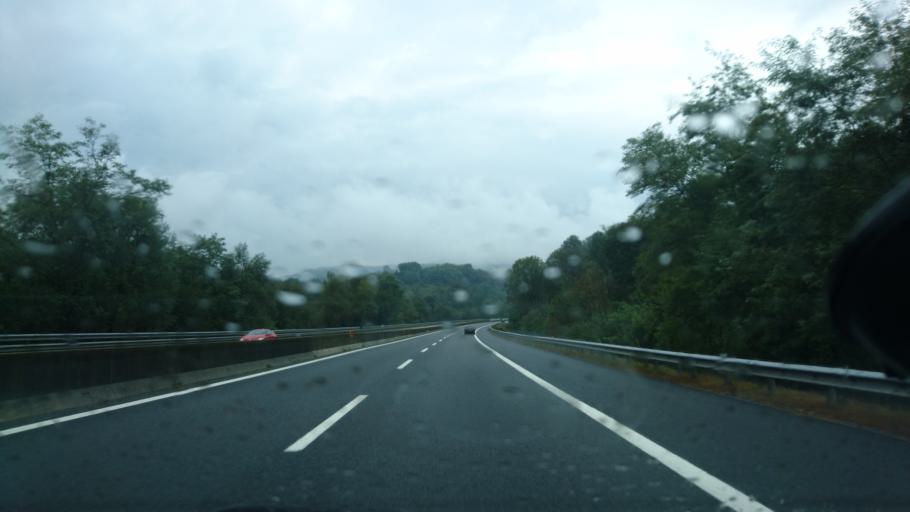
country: IT
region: Piedmont
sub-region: Provincia di Novara
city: Invorio
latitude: 45.7620
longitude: 8.4981
